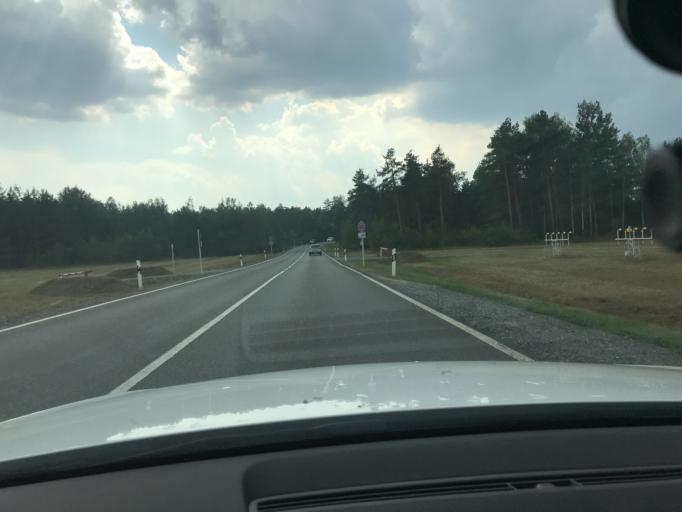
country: DE
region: Bavaria
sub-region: Upper Palatinate
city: Grafenwohr
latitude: 49.7046
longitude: 11.9343
